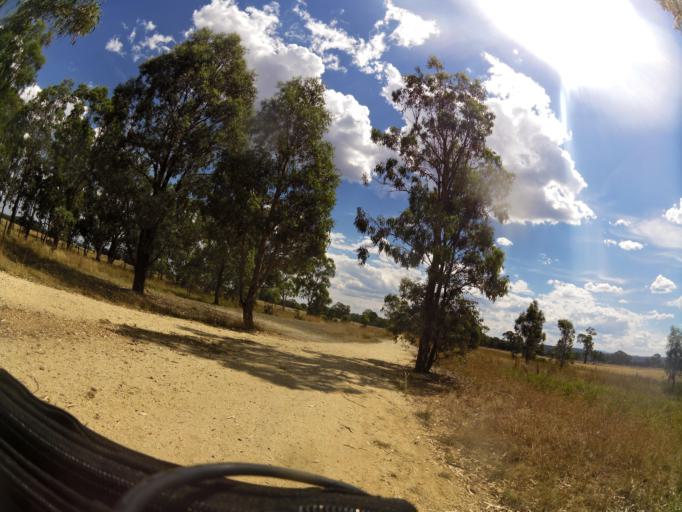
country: AU
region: Victoria
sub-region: Wellington
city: Heyfield
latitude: -37.9836
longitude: 146.7242
